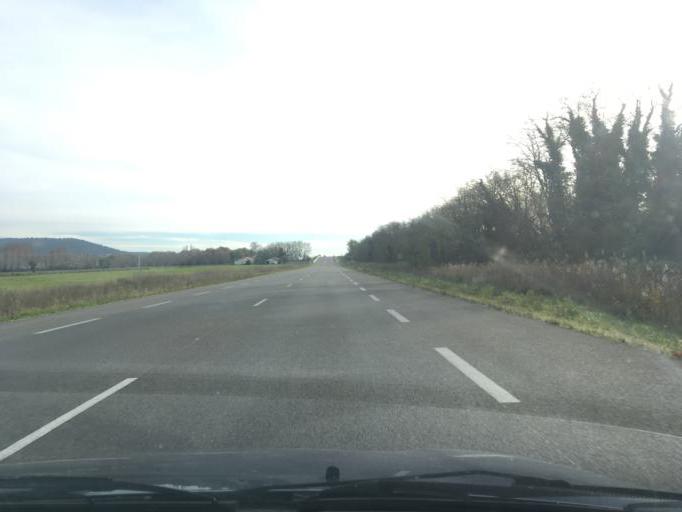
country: FR
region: Provence-Alpes-Cote d'Azur
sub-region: Departement du Vaucluse
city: Villelaure
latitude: 43.7157
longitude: 5.4051
